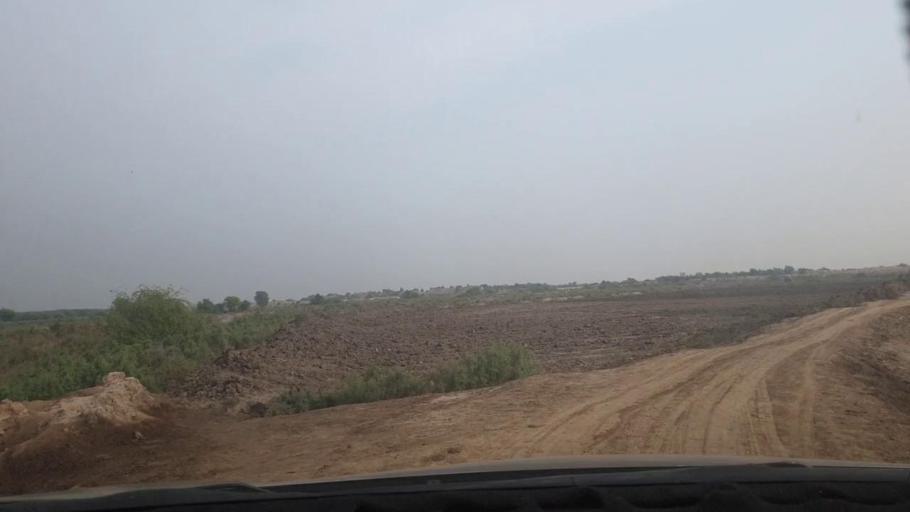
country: PK
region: Sindh
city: Jamshoro
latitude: 25.5211
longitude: 68.3209
